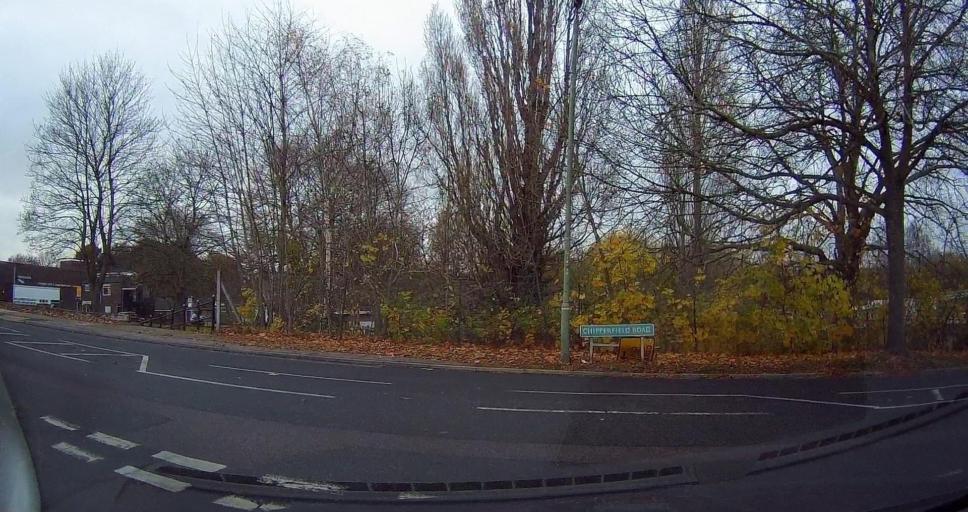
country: GB
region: England
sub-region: Greater London
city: Sidcup
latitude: 51.4046
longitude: 0.1042
